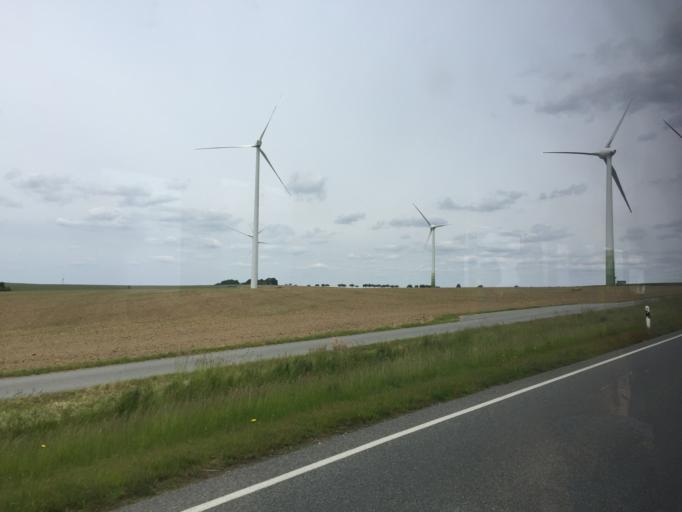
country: DE
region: Saxony
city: Sohland am Rotstein
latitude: 51.1405
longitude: 14.7716
